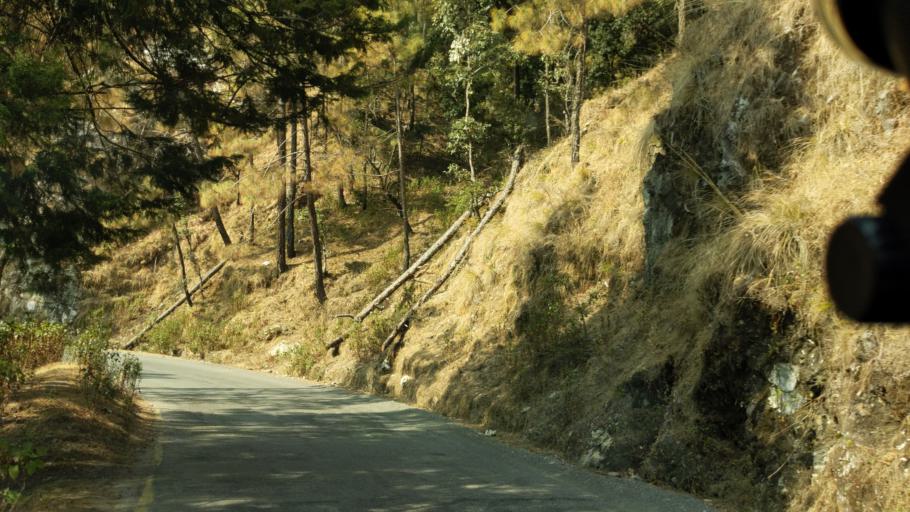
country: IN
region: Uttarakhand
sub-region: Naini Tal
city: Bhowali
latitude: 29.4027
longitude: 79.5383
